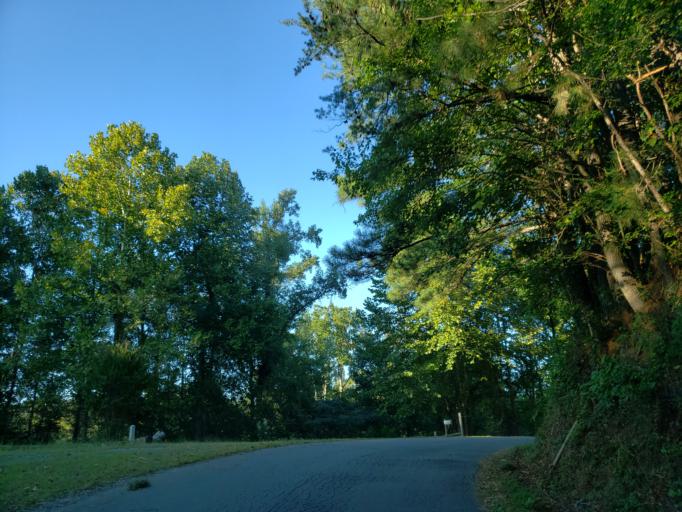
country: US
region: Georgia
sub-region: Bartow County
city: Rydal
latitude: 34.4066
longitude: -84.6799
